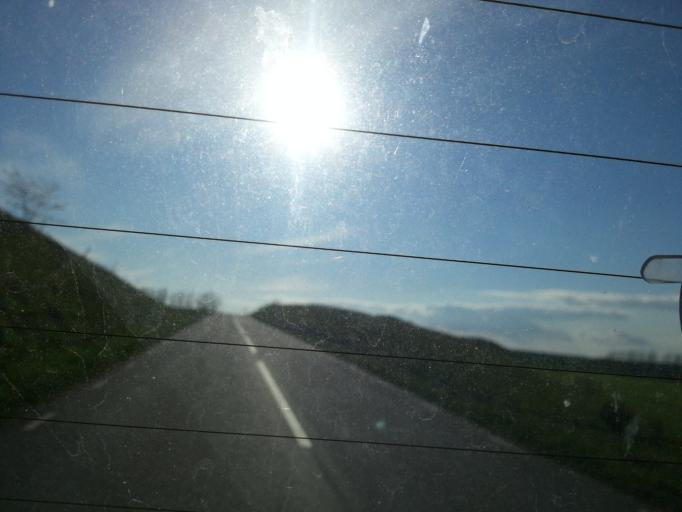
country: SE
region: Skane
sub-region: Ystads Kommun
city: Kopingebro
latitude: 55.3901
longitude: 14.0694
